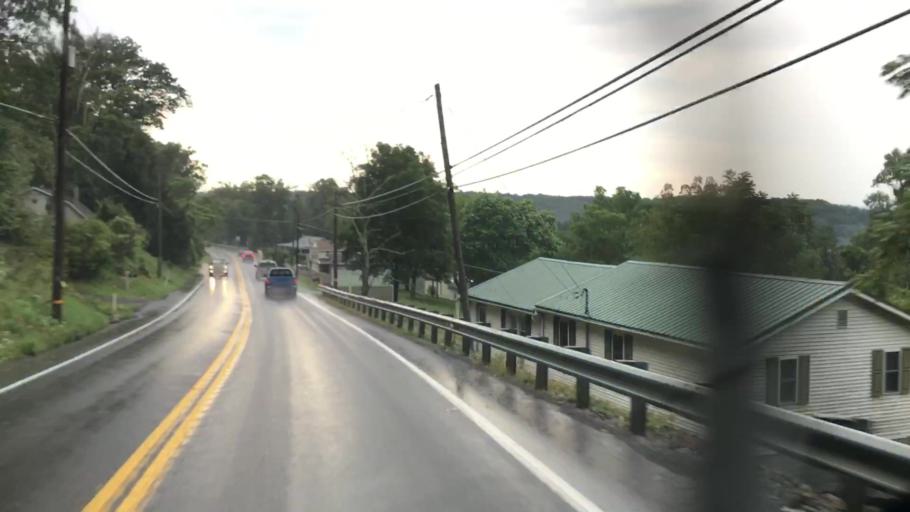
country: US
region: Pennsylvania
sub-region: Cumberland County
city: Schlusser
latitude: 40.2971
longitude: -77.1348
